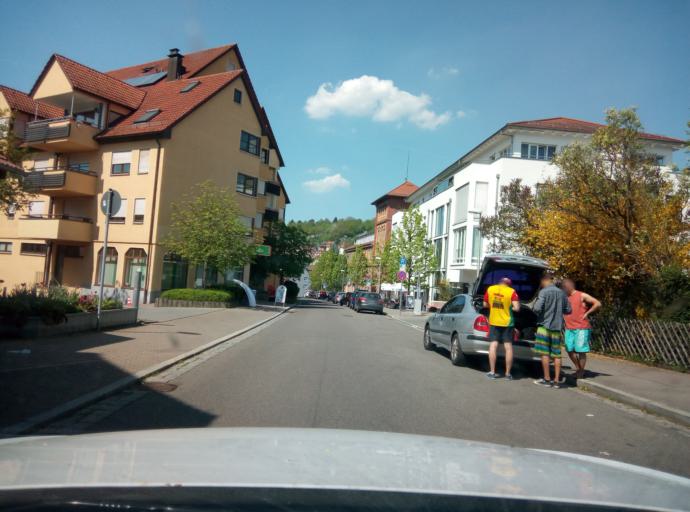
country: DE
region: Baden-Wuerttemberg
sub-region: Tuebingen Region
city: Tuebingen
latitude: 48.5305
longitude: 9.0811
